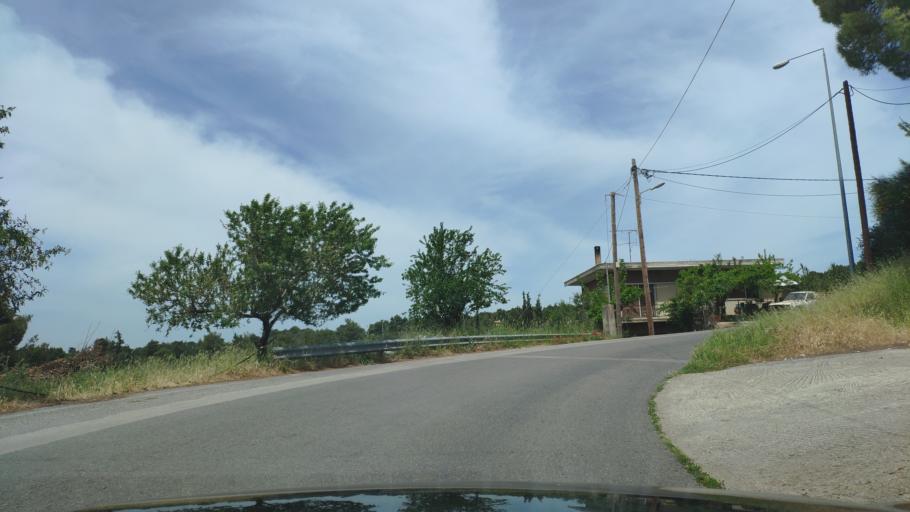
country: GR
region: Attica
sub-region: Nomarchia Anatolikis Attikis
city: Varnavas
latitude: 38.2198
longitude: 23.9187
